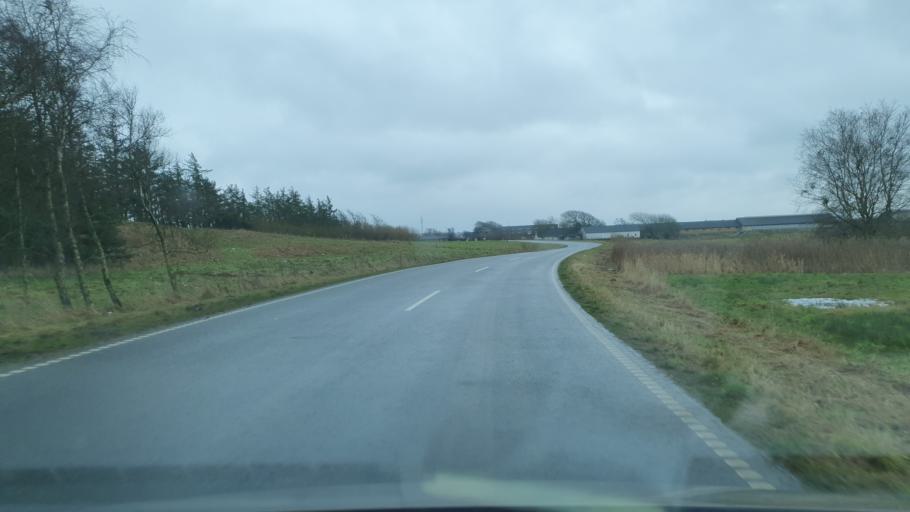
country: DK
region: North Denmark
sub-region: Jammerbugt Kommune
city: Fjerritslev
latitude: 57.1141
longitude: 9.1285
